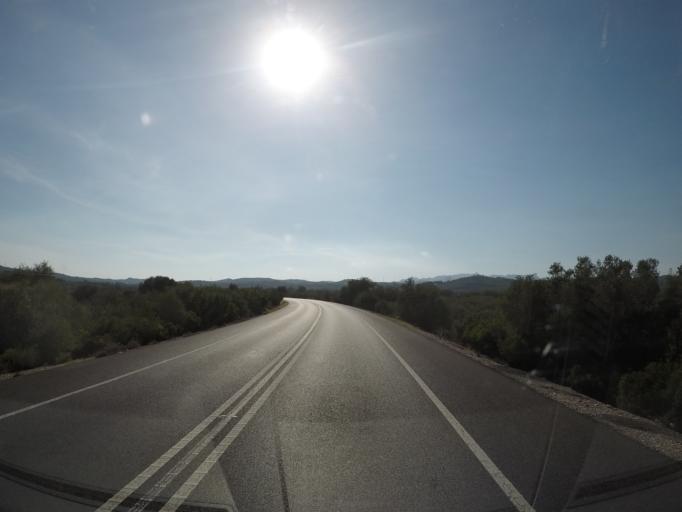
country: ES
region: Catalonia
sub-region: Provincia de Tarragona
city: El Perello
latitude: 40.8973
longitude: 0.7321
